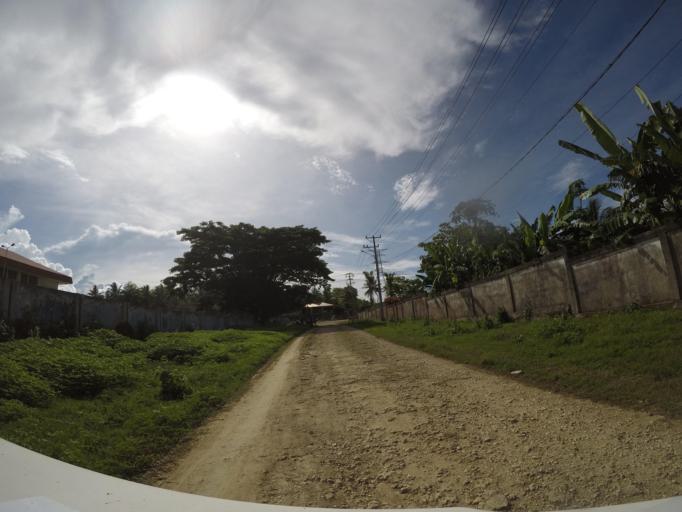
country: TL
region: Lautem
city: Lospalos
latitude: -8.4922
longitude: 126.9936
